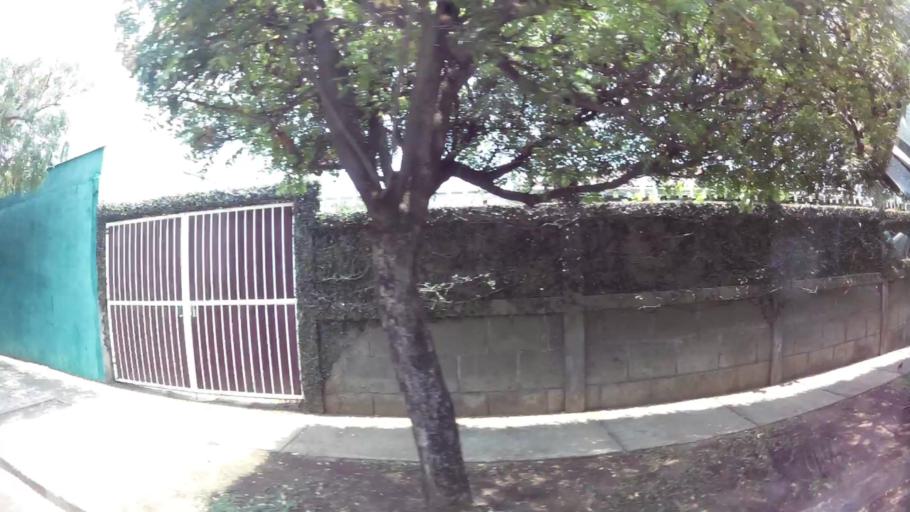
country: NI
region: Managua
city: Managua
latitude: 12.1199
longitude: -86.2857
